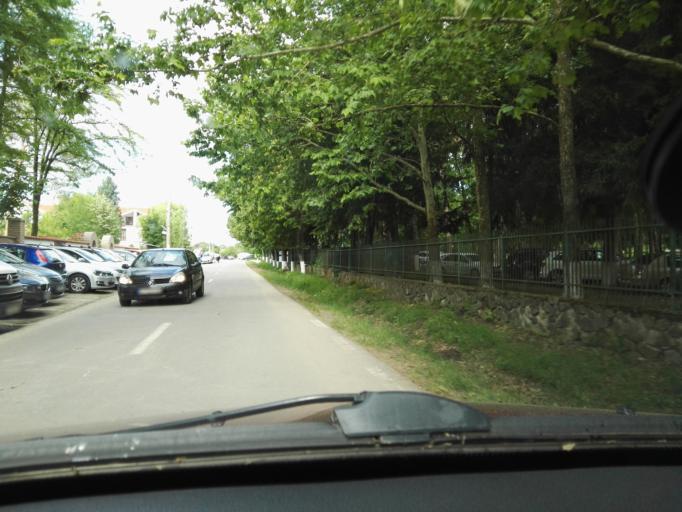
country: RO
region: Giurgiu
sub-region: Comuna Comana
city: Comana
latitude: 44.1717
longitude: 26.1341
